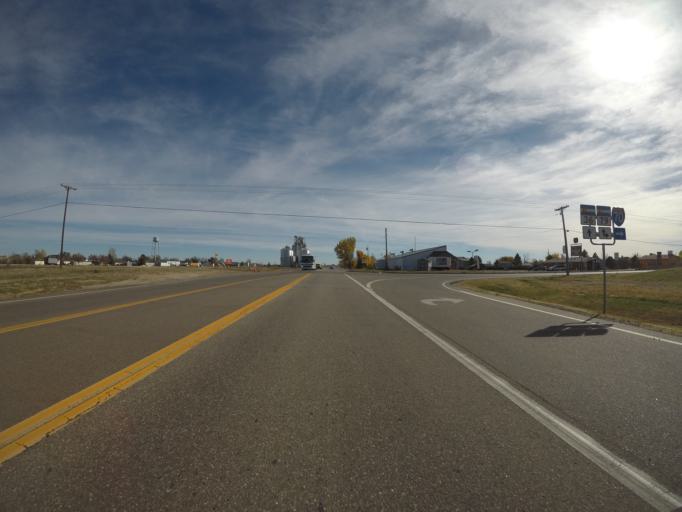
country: US
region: Colorado
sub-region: Adams County
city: Bennett
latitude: 39.7559
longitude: -104.4338
